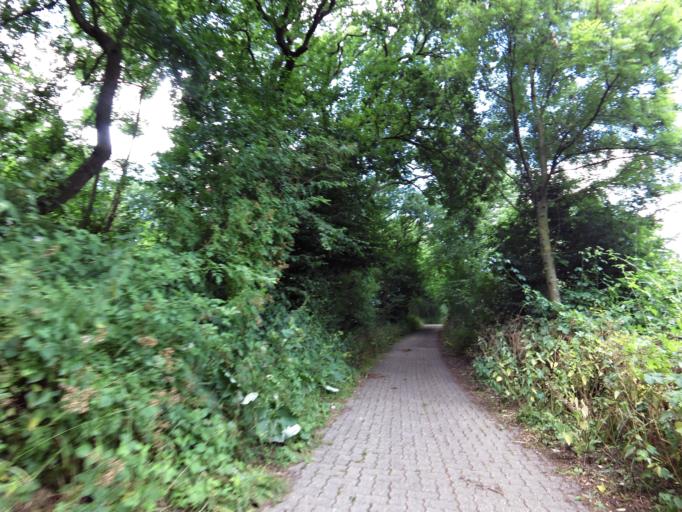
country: DE
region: North Rhine-Westphalia
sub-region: Regierungsbezirk Koln
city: Herzogenrath
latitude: 50.8563
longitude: 6.0874
